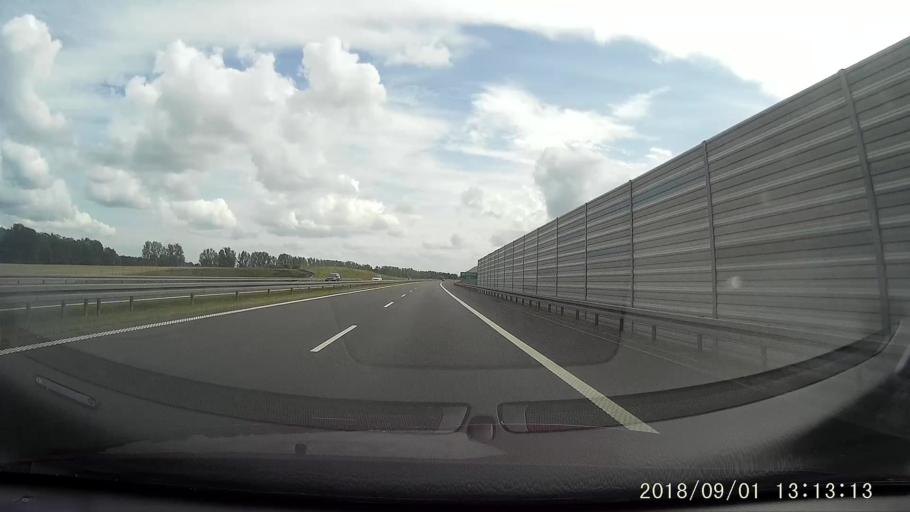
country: PL
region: West Pomeranian Voivodeship
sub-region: Powiat gryfinski
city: Gryfino
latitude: 53.2935
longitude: 14.5983
